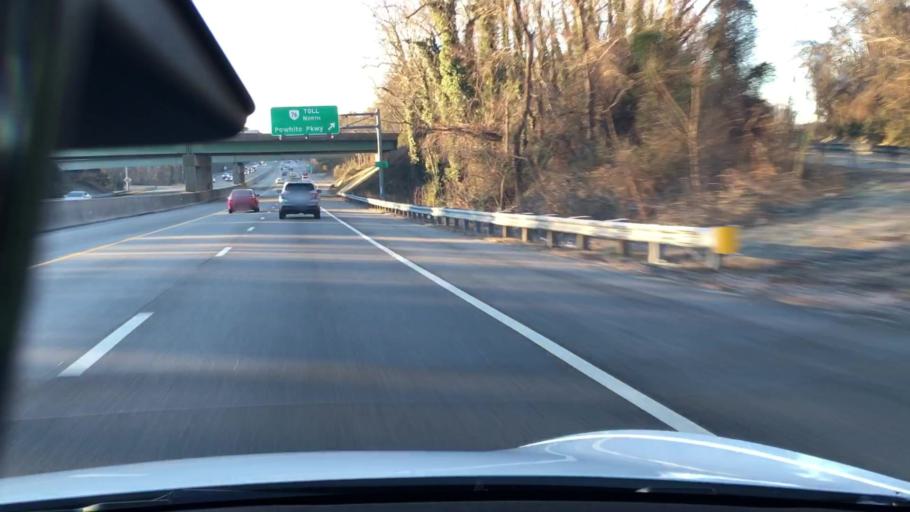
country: US
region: Virginia
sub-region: Chesterfield County
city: Bon Air
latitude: 37.5271
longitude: -77.5287
